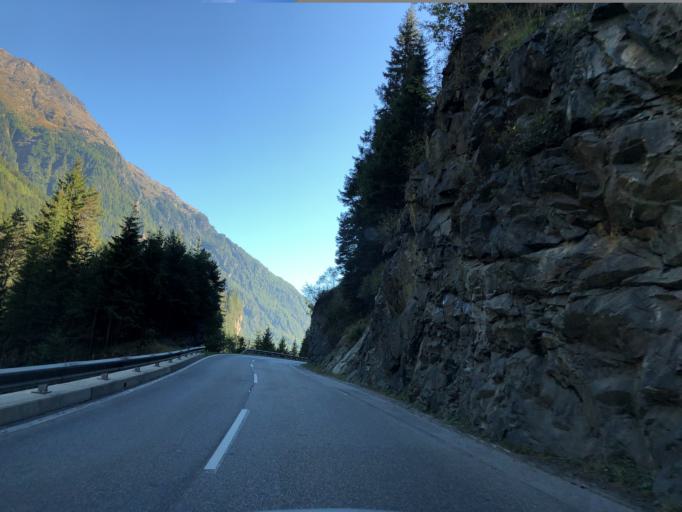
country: AT
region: Tyrol
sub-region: Politischer Bezirk Imst
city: Soelden
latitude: 47.0016
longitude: 11.0089
